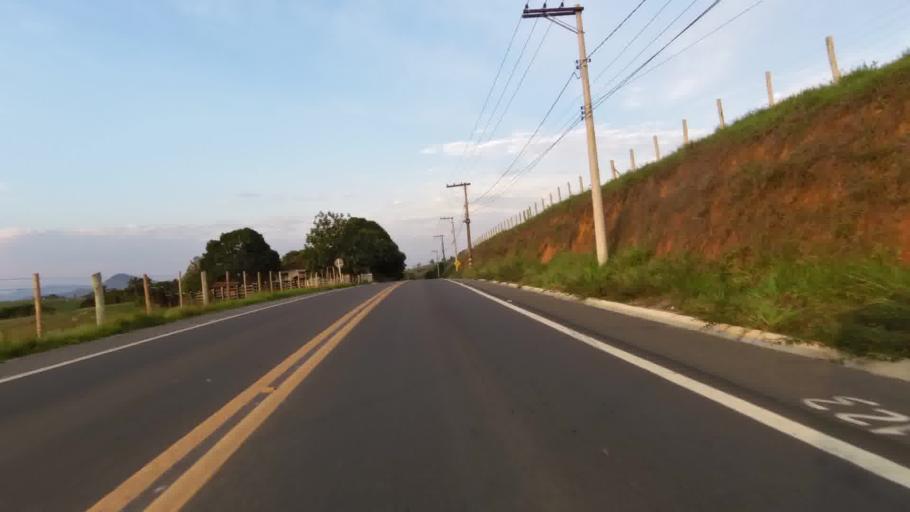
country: BR
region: Espirito Santo
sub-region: Piuma
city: Piuma
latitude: -20.8062
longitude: -40.6760
